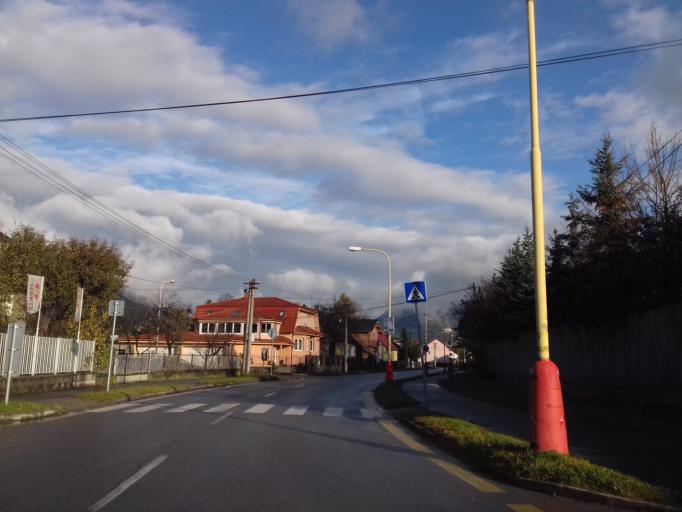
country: SK
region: Zilinsky
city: Ruzomberok
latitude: 49.0730
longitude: 19.3092
